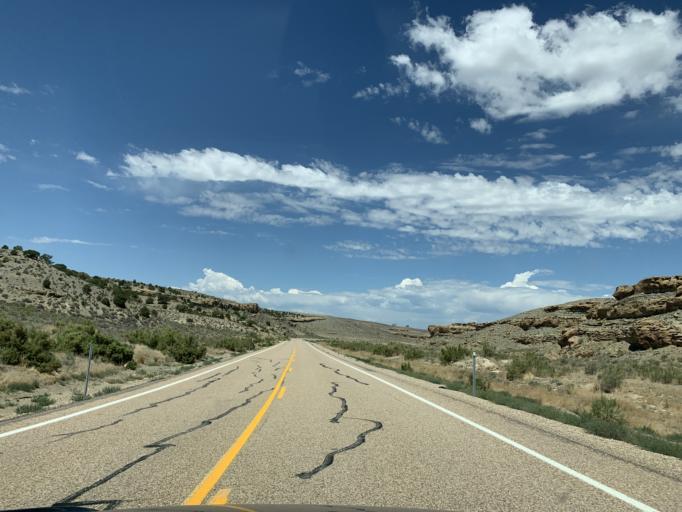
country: US
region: Utah
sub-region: Duchesne County
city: Duchesne
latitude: 40.0144
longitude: -110.1523
